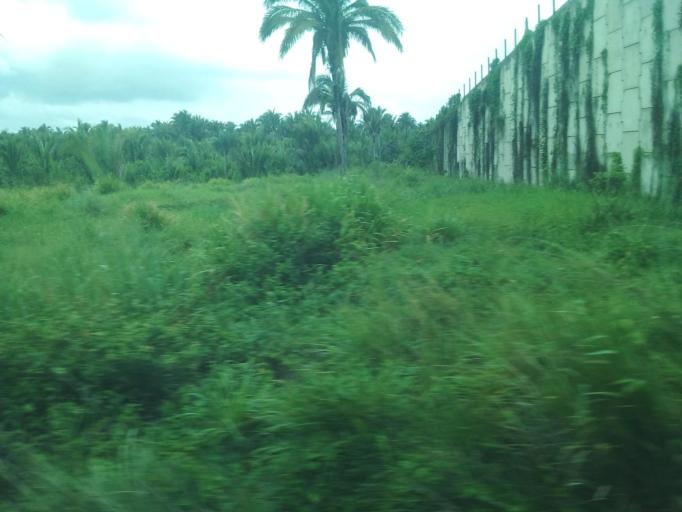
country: BR
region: Maranhao
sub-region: Moncao
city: Moncao
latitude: -3.6110
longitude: -45.1595
